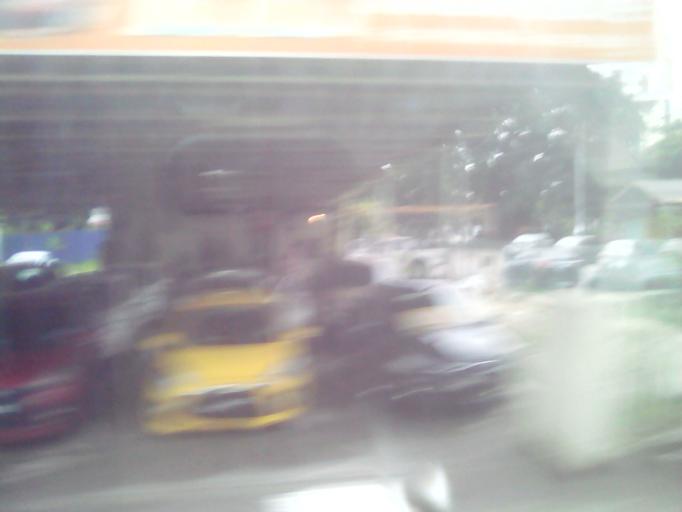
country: MY
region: Penang
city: Butterworth
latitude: 5.3977
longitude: 100.3700
